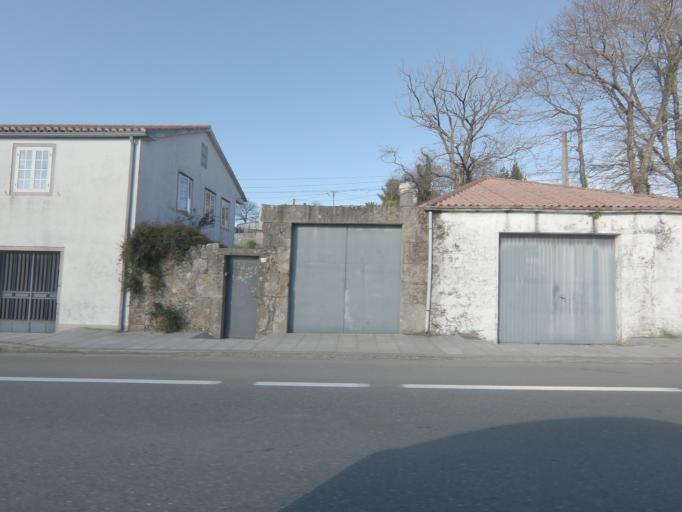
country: ES
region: Galicia
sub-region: Provincia de Pontevedra
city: Silleda
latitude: 42.7018
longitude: -8.2573
